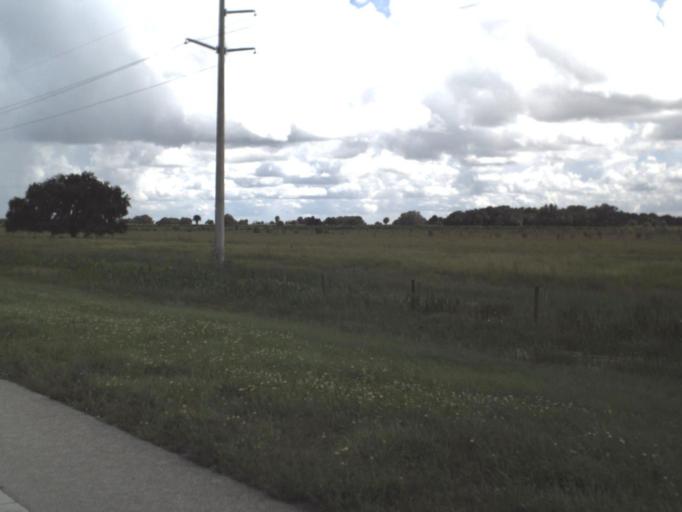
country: US
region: Florida
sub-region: DeSoto County
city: Southeast Arcadia
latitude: 27.2095
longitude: -81.6480
